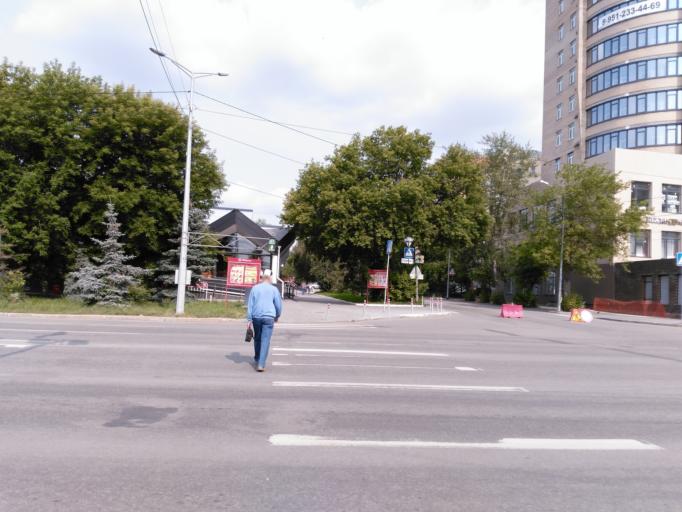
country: RU
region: Chelyabinsk
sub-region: Gorod Chelyabinsk
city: Chelyabinsk
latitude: 55.1632
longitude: 61.4110
